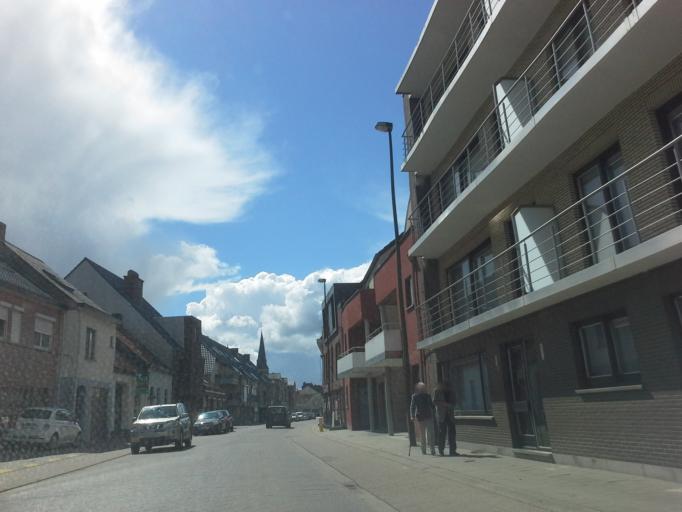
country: BE
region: Flanders
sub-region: Provincie Limburg
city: Tessenderlo
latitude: 51.0717
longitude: 5.0892
